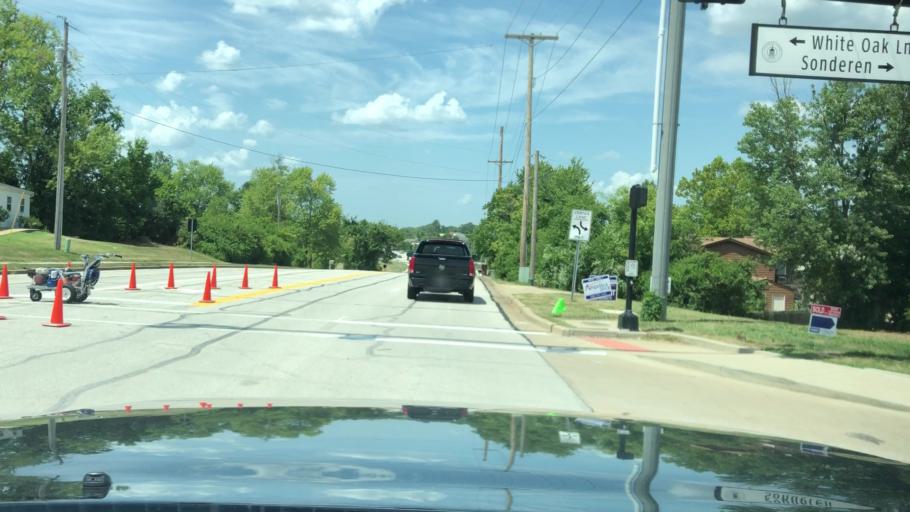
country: US
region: Missouri
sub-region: Saint Charles County
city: O'Fallon
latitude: 38.7917
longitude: -90.6913
